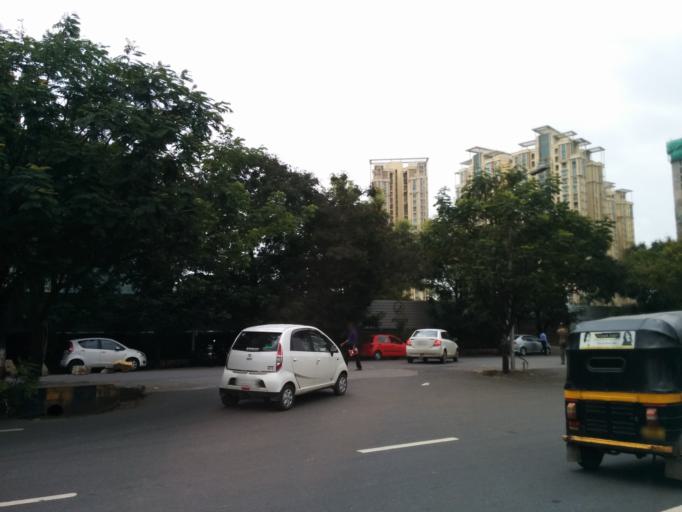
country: IN
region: Maharashtra
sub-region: Thane
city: Thane
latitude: 19.2093
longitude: 72.9735
